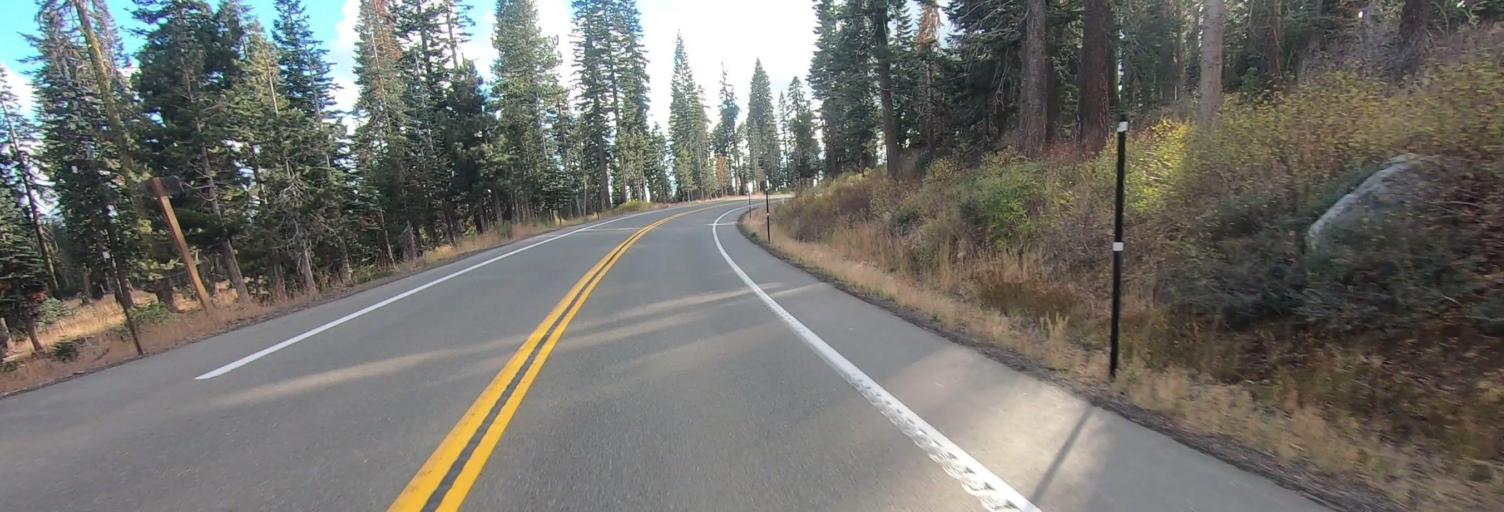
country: US
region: California
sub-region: Calaveras County
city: Arnold
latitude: 38.5884
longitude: -120.2312
